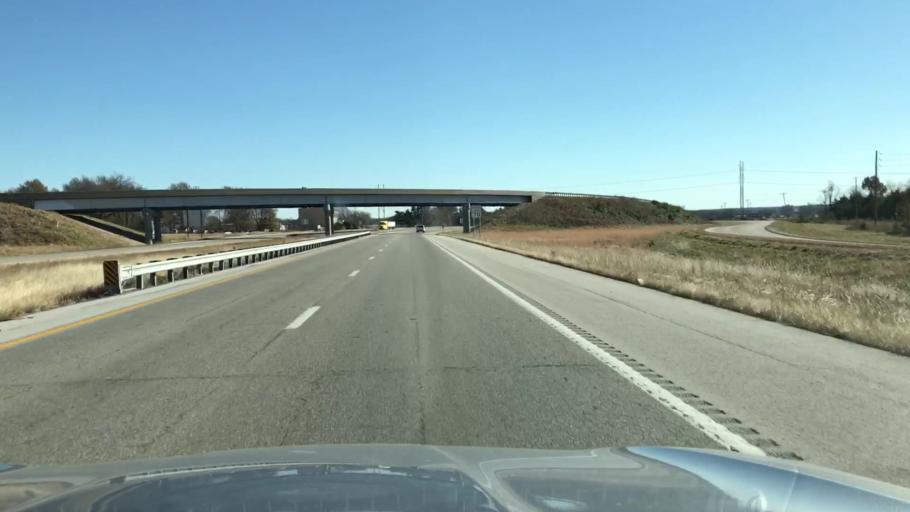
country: US
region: Missouri
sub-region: Jasper County
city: Carthage
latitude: 37.1339
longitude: -94.3151
